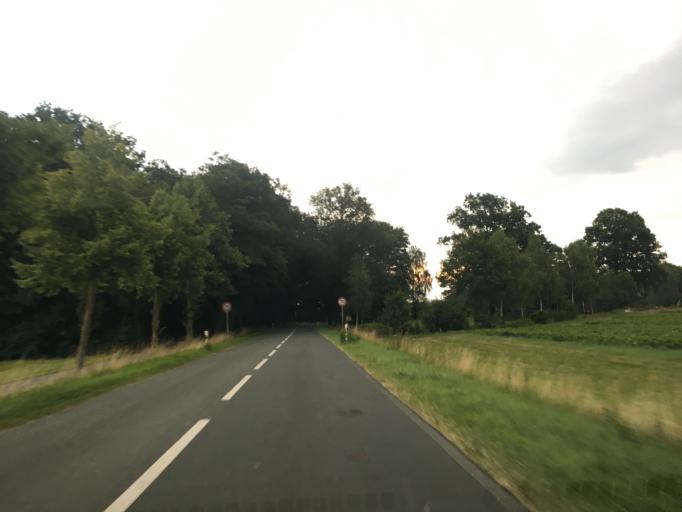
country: DE
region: North Rhine-Westphalia
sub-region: Regierungsbezirk Munster
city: Senden
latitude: 51.8611
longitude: 7.5130
